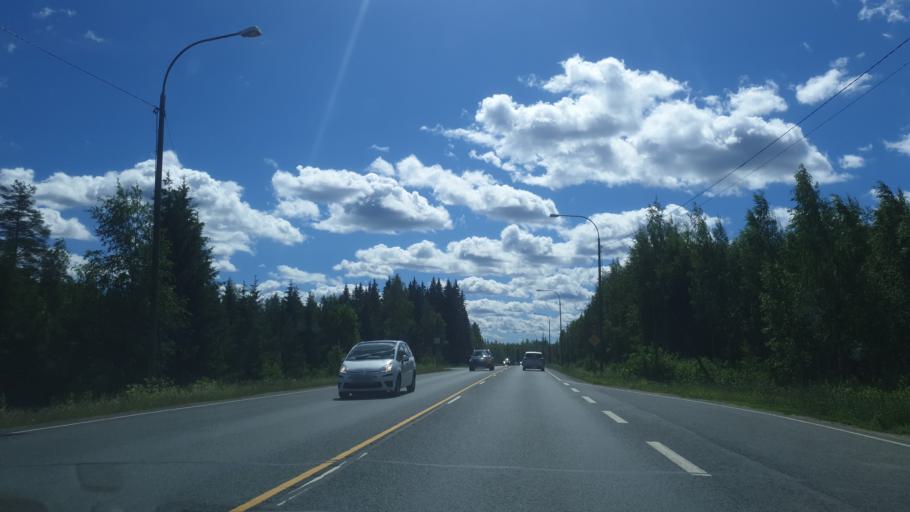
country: FI
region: Northern Savo
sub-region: Varkaus
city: Leppaevirta
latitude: 62.5501
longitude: 27.6221
